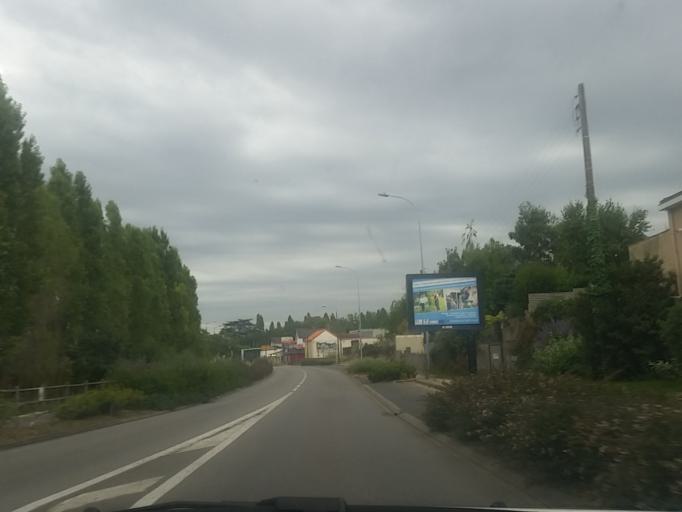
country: FR
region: Pays de la Loire
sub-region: Departement de la Loire-Atlantique
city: Saint-Sebastien-sur-Loire
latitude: 47.2099
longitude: -1.5043
